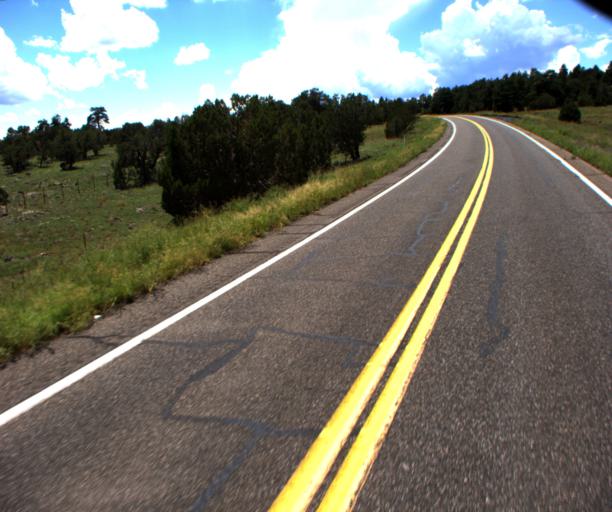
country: US
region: Arizona
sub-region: Gila County
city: Pine
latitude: 34.5141
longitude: -111.5380
